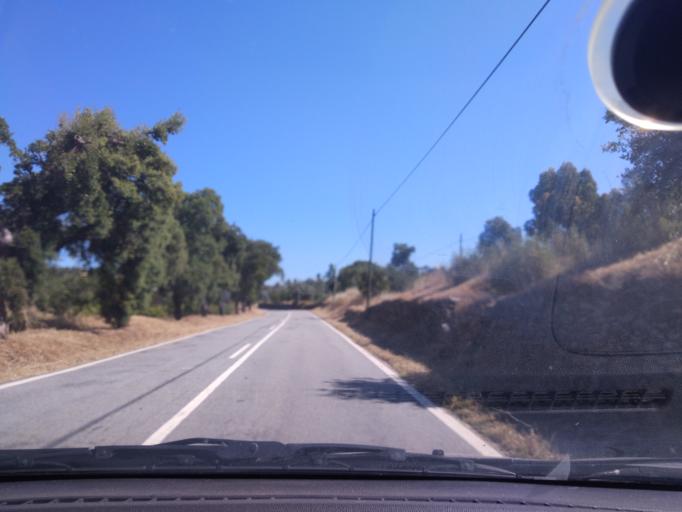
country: ES
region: Extremadura
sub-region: Provincia de Caceres
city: Cedillo
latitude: 39.7406
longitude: -7.6210
